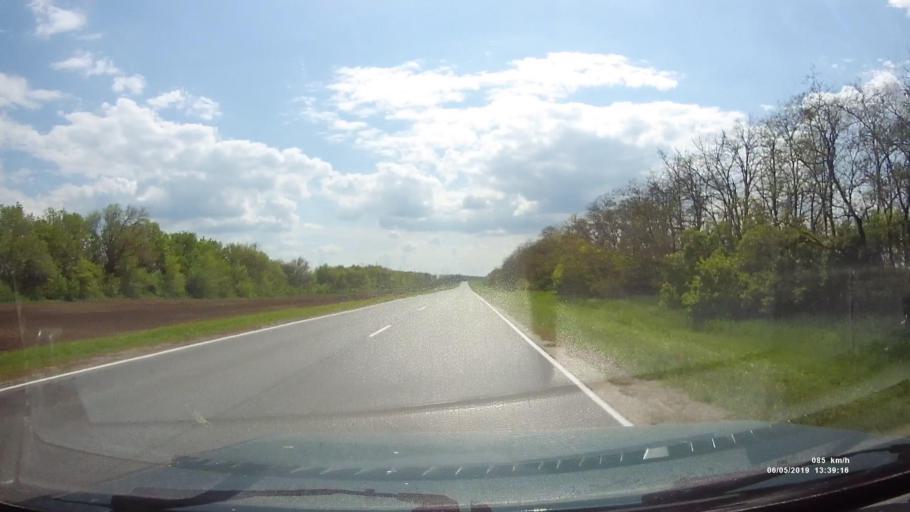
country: RU
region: Rostov
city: Ust'-Donetskiy
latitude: 47.6779
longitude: 40.7042
